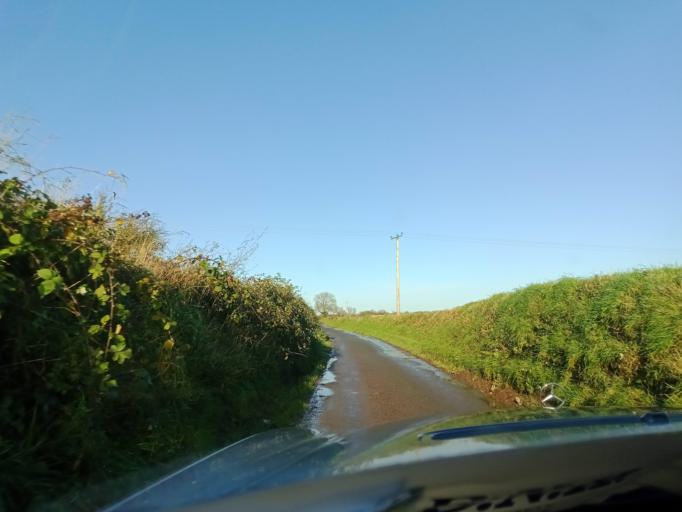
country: IE
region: Munster
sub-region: Waterford
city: Waterford
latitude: 52.2853
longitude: -7.1658
